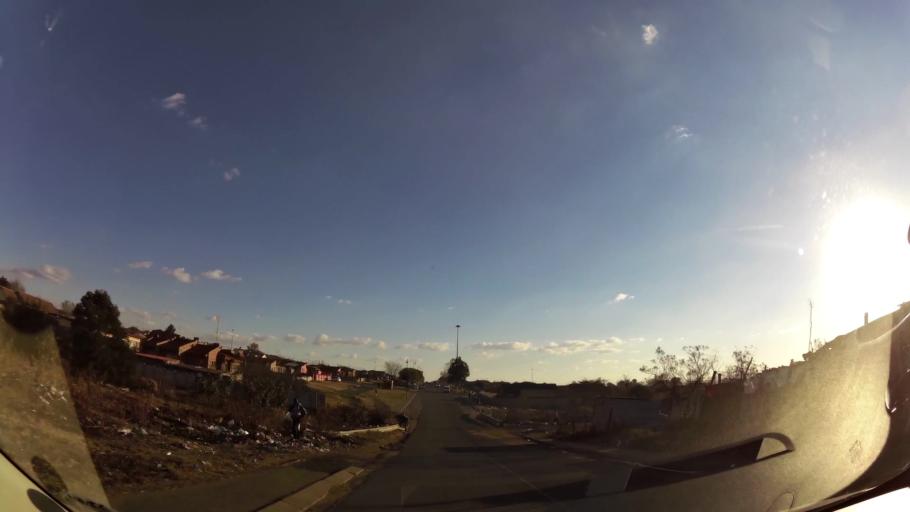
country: ZA
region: Mpumalanga
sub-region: Nkangala District Municipality
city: Witbank
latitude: -25.8776
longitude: 29.1975
